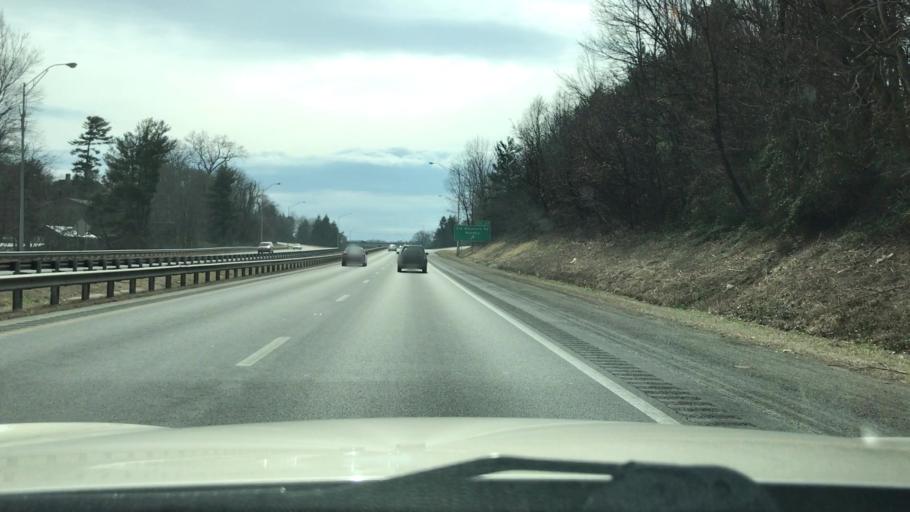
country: US
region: North Carolina
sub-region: Buncombe County
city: Woodfin
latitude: 35.6364
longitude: -82.5808
